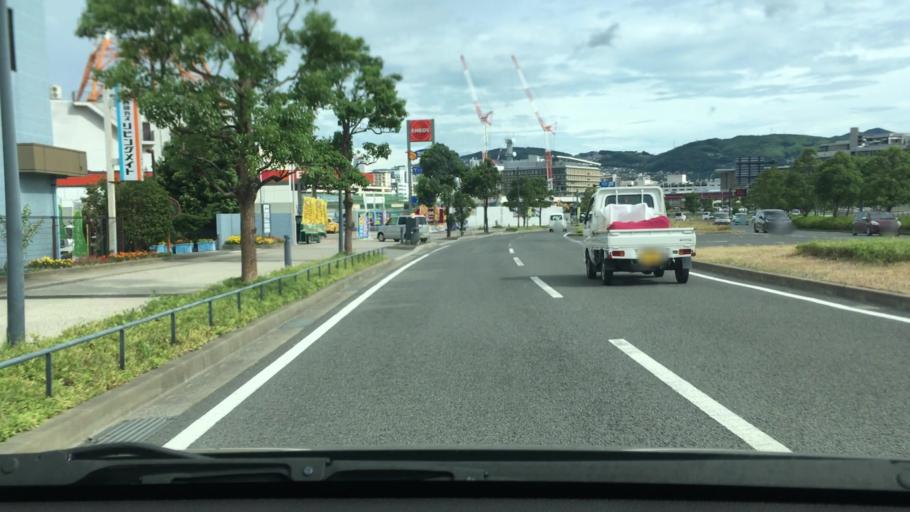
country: JP
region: Nagasaki
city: Nagasaki-shi
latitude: 32.7554
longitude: 129.8665
